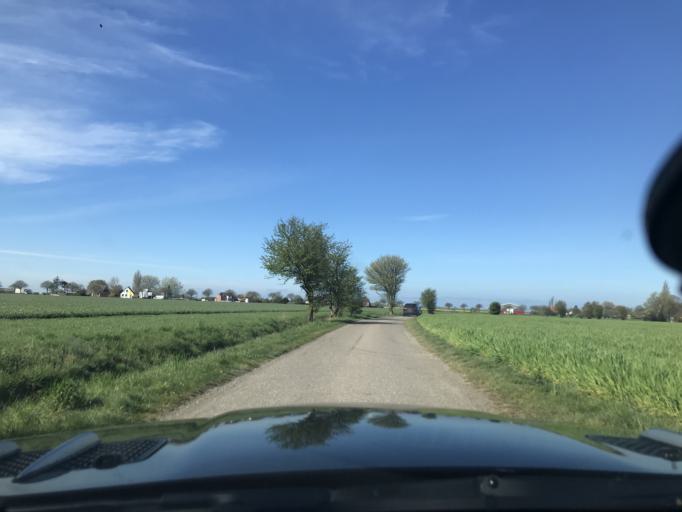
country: DE
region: Schleswig-Holstein
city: Grossenbrode
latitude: 54.4562
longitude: 11.0528
